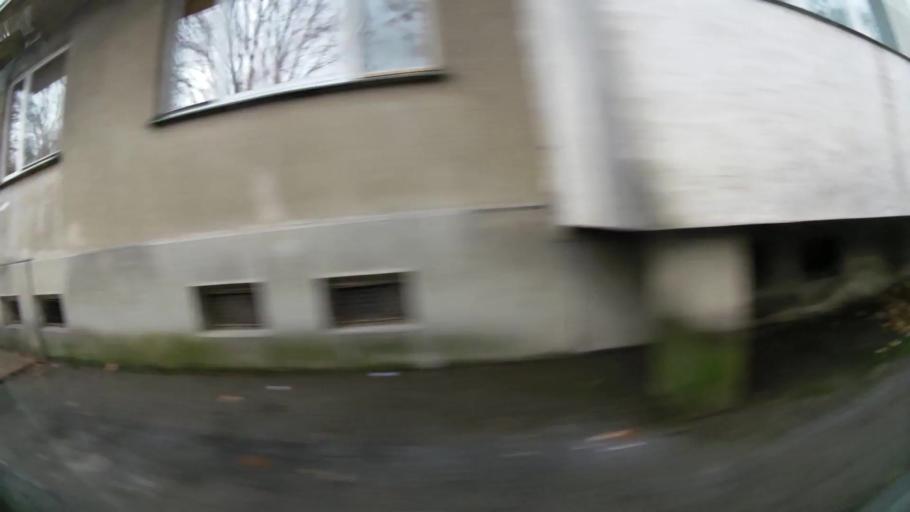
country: BG
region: Sofia-Capital
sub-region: Stolichna Obshtina
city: Sofia
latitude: 42.7356
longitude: 23.3038
